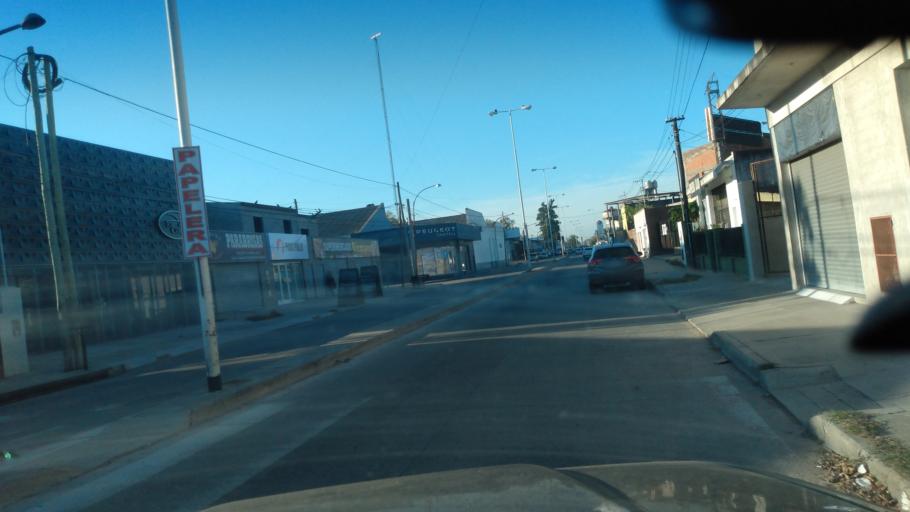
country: AR
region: Buenos Aires
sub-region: Partido de Lujan
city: Lujan
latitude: -34.5674
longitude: -59.0960
